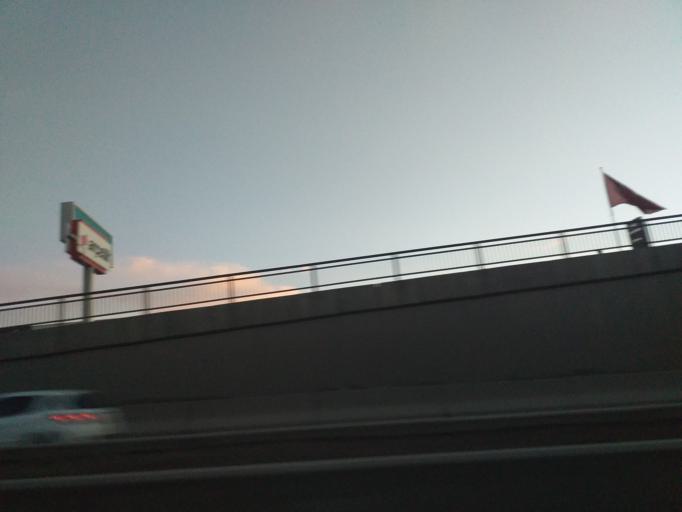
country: TR
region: Ankara
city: Batikent
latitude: 39.9456
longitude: 32.7131
